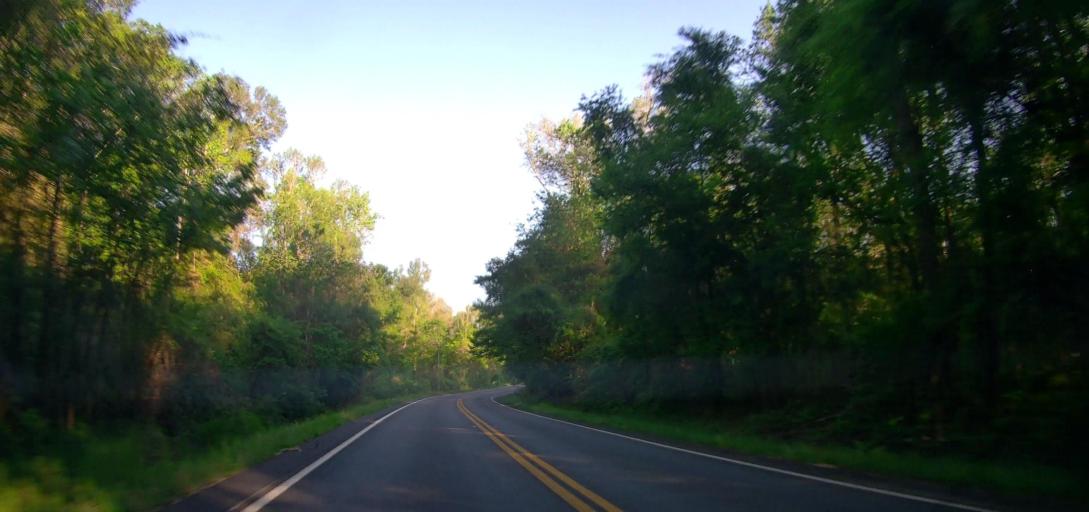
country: US
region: Georgia
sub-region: Macon County
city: Oglethorpe
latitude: 32.3026
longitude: -84.1575
